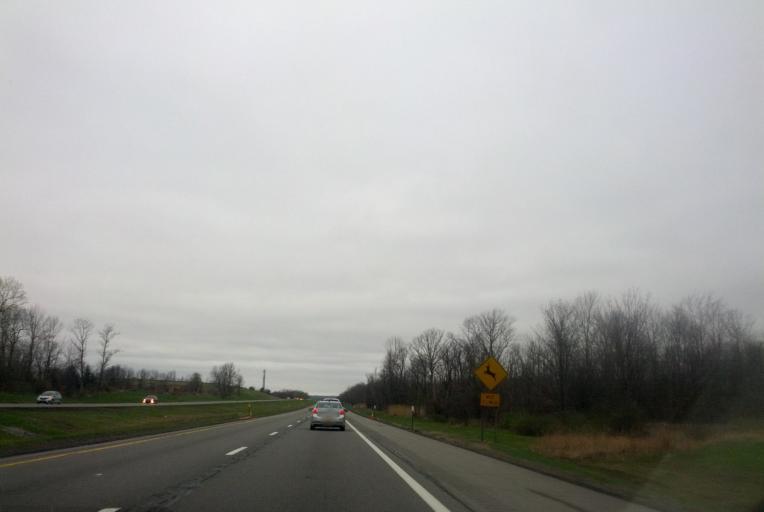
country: US
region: New York
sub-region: Ontario County
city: Manchester
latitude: 42.9878
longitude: -77.3091
